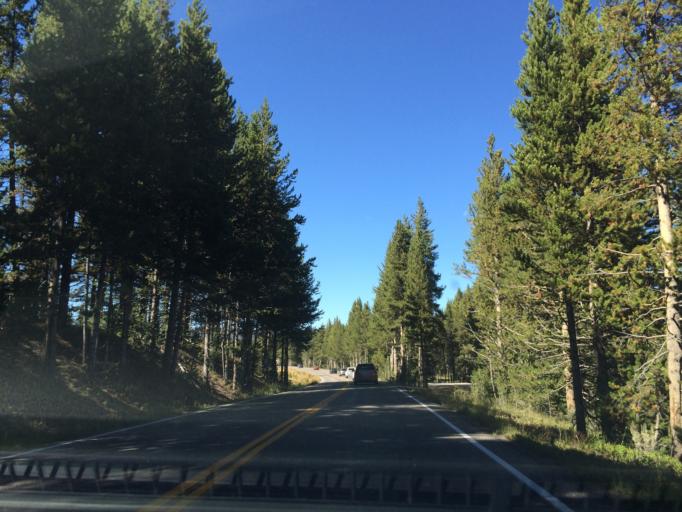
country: US
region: Montana
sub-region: Gallatin County
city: West Yellowstone
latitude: 44.6932
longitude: -110.4997
